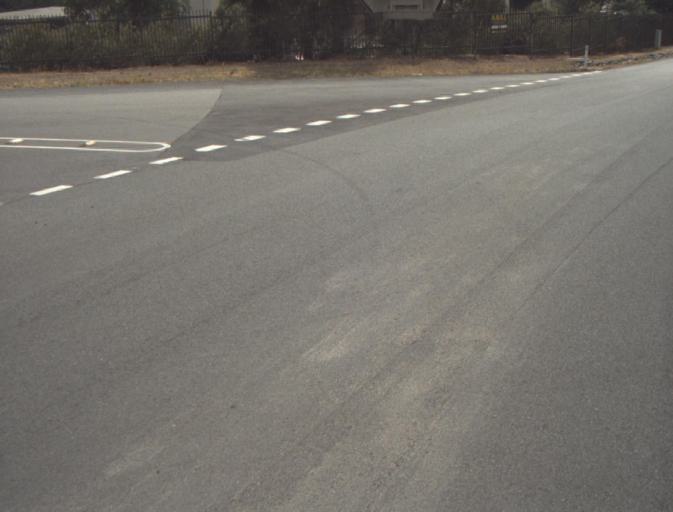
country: AU
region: Tasmania
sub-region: Launceston
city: Summerhill
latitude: -41.4800
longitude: 147.1544
